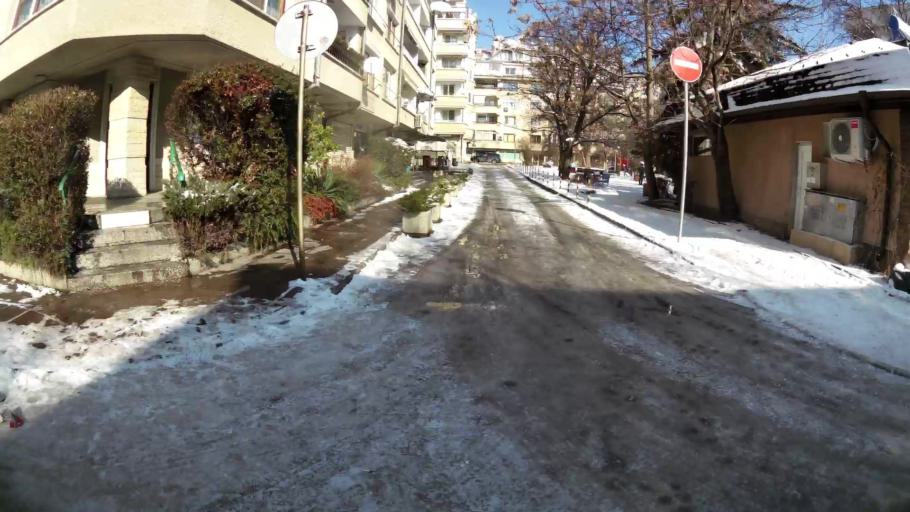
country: BG
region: Sofia-Capital
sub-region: Stolichna Obshtina
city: Sofia
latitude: 42.6692
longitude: 23.3170
